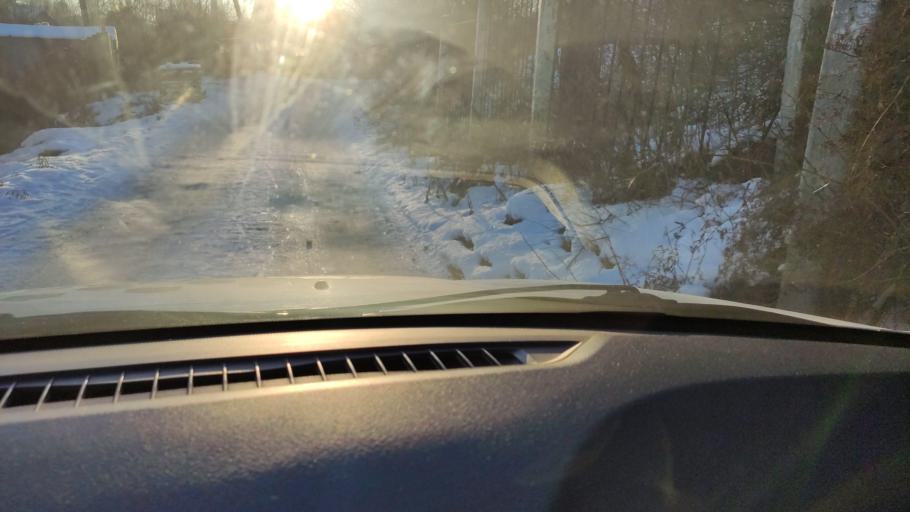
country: RU
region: Perm
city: Perm
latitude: 58.0327
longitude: 56.3324
